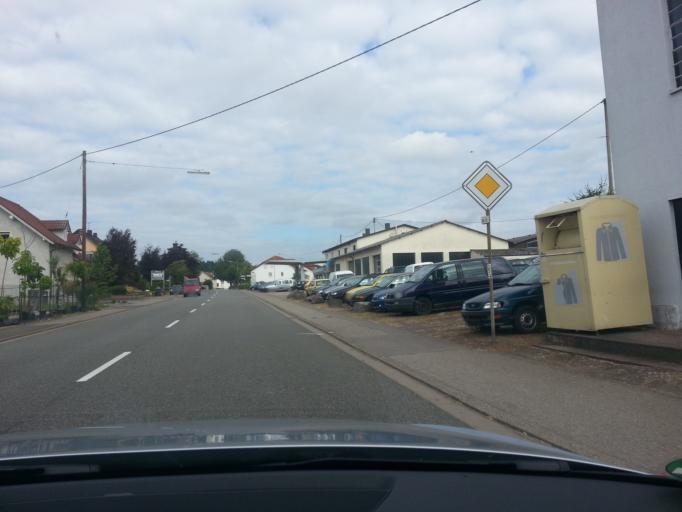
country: DE
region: Saarland
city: Losheim
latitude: 49.5120
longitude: 6.7393
